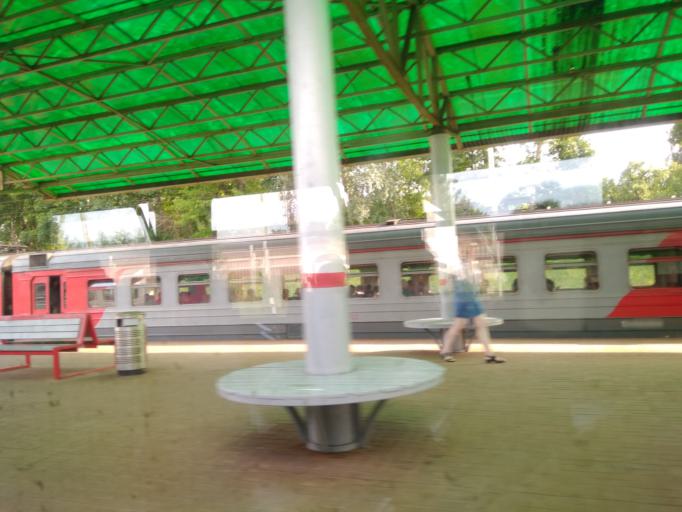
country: RU
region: Moskovskaya
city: Kraskovo
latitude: 55.6497
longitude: 37.9830
